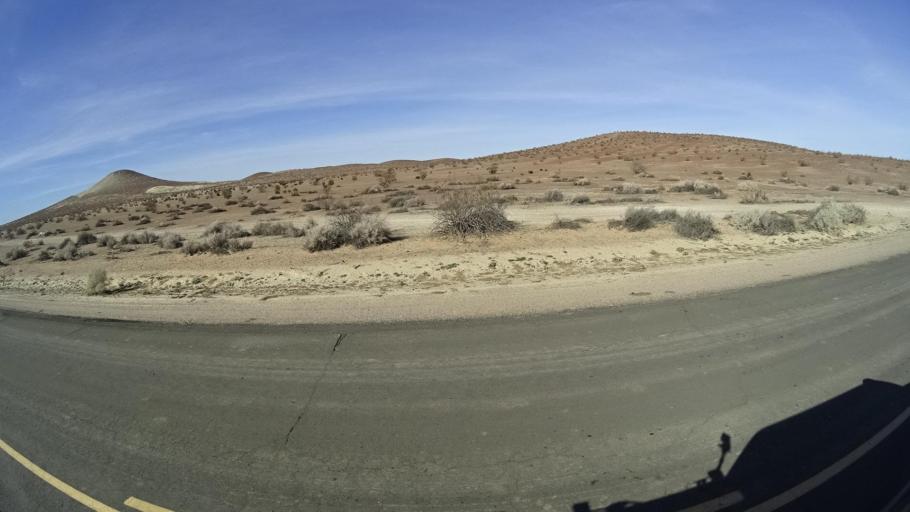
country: US
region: California
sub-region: Kern County
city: North Edwards
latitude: 35.0591
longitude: -117.8083
